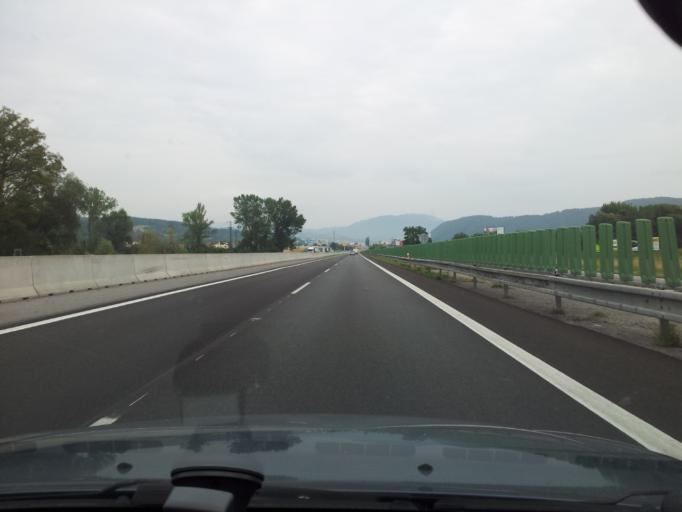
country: SK
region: Banskobystricky
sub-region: Okres Banska Bystrica
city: Banska Bystrica
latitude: 48.6894
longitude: 19.1320
